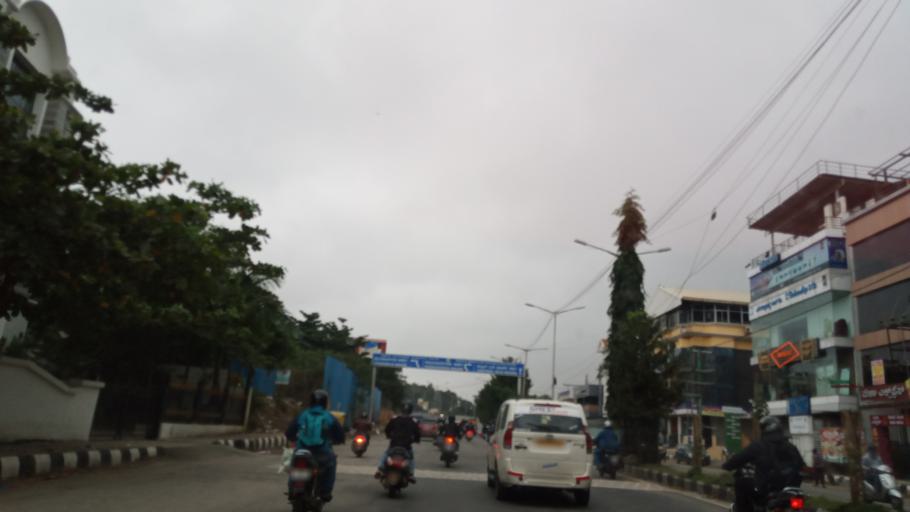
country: IN
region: Karnataka
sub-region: Bangalore Urban
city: Bangalore
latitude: 12.9226
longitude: 77.5574
